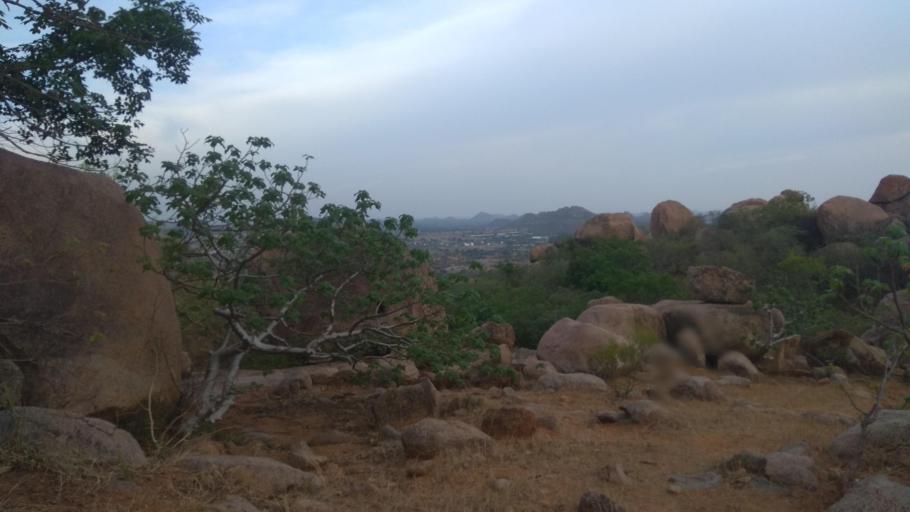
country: IN
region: Telangana
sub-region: Mahbubnagar
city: Farrukhnagar
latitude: 16.8885
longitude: 78.5073
